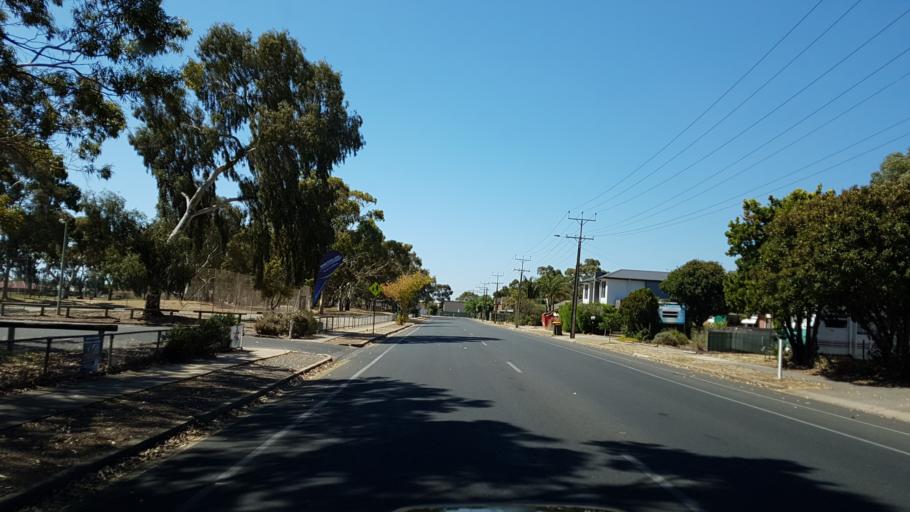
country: AU
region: South Australia
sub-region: Marion
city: Clovelly Park
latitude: -35.0026
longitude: 138.5655
